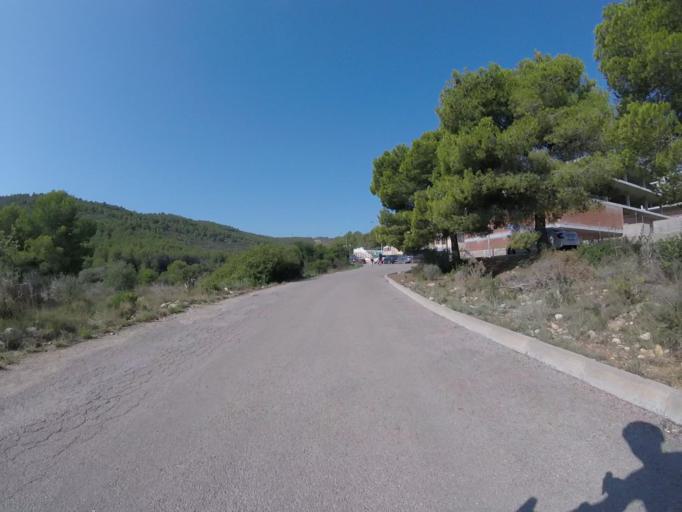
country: ES
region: Valencia
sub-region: Provincia de Castello
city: Peniscola
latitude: 40.3325
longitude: 0.3652
